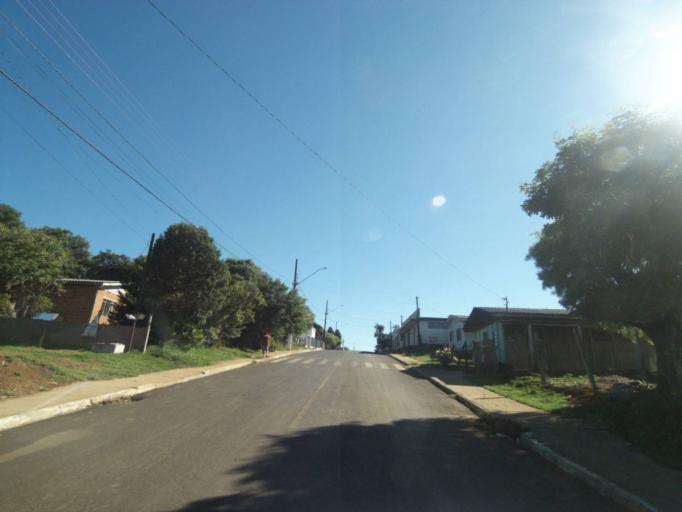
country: BR
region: Parana
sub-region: Pinhao
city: Pinhao
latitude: -25.8395
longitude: -52.0302
